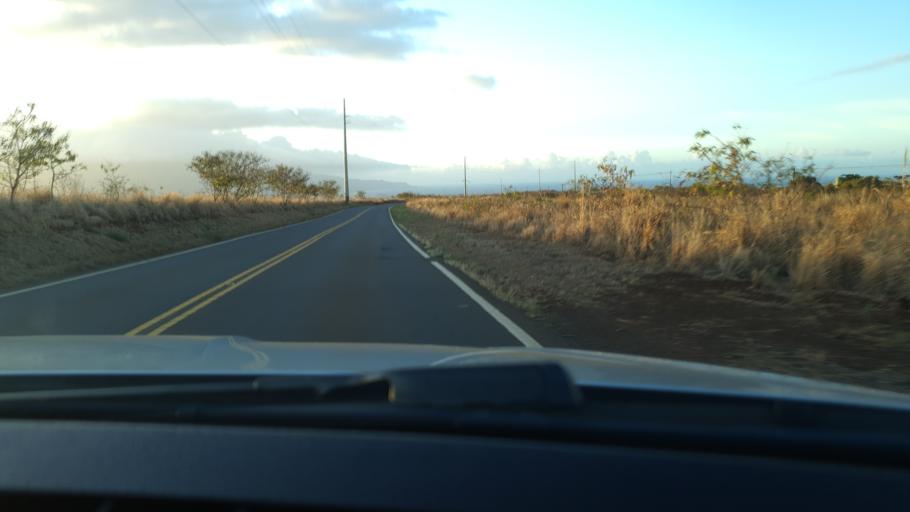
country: US
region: Hawaii
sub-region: Maui County
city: Pukalani
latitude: 20.8154
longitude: -156.3855
